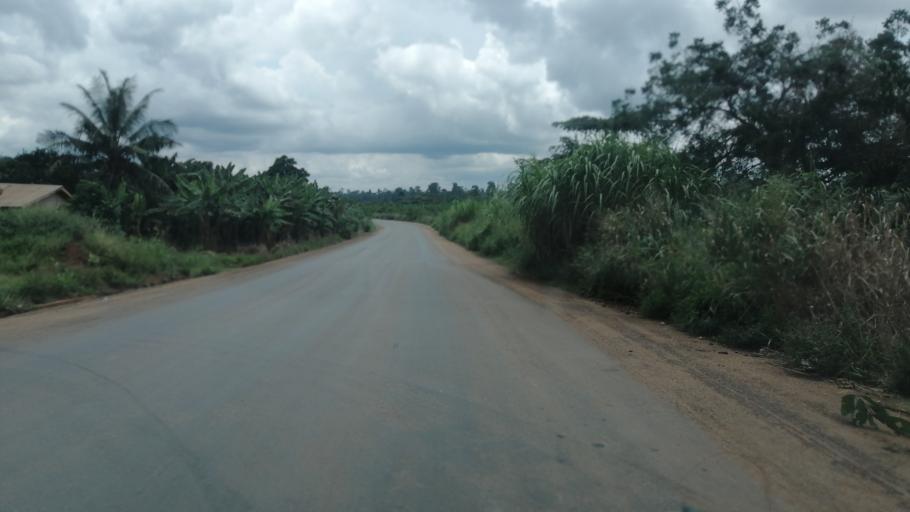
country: GH
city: Duayaw Nkwanta
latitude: 6.9119
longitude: -2.3907
